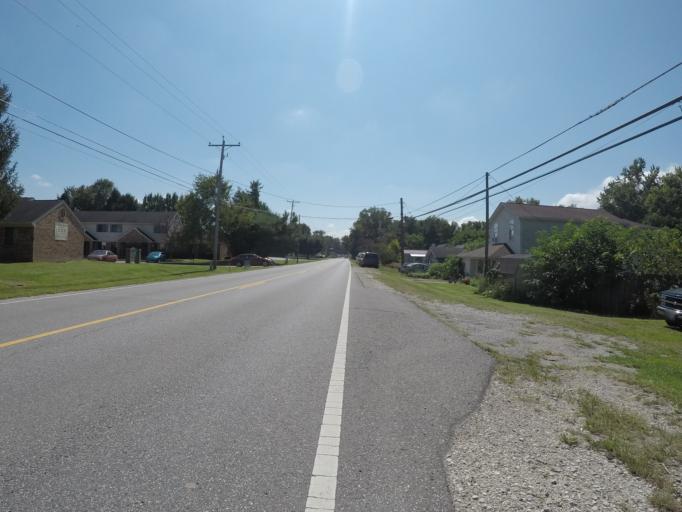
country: US
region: Ohio
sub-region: Lawrence County
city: South Point
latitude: 38.4550
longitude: -82.5960
